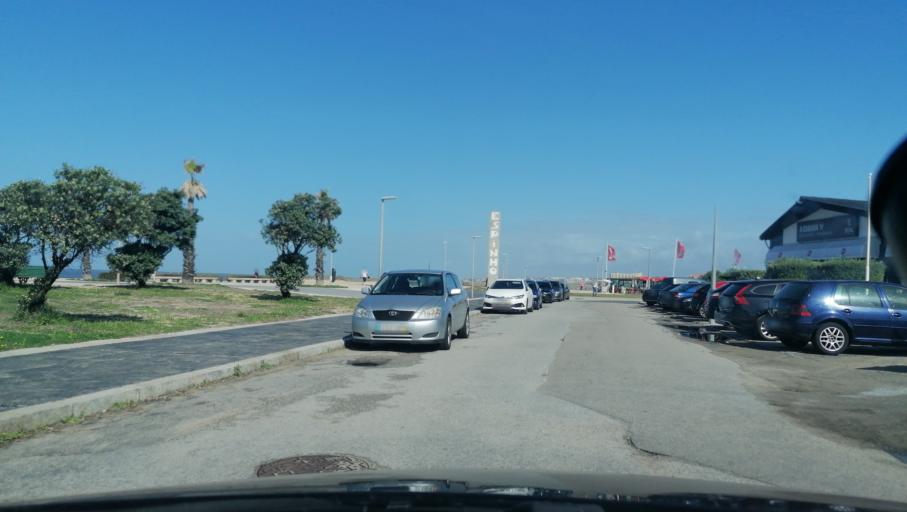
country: PT
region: Aveiro
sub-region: Espinho
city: Espinho
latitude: 41.0138
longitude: -8.6445
